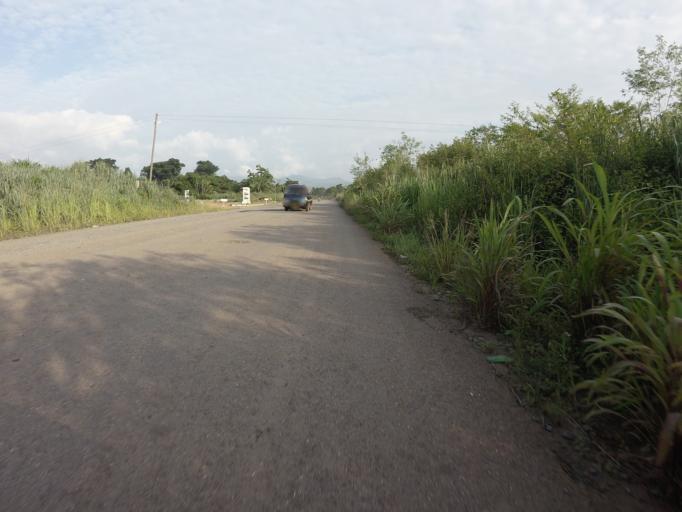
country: GH
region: Volta
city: Kpandu
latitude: 6.9806
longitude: 0.4480
